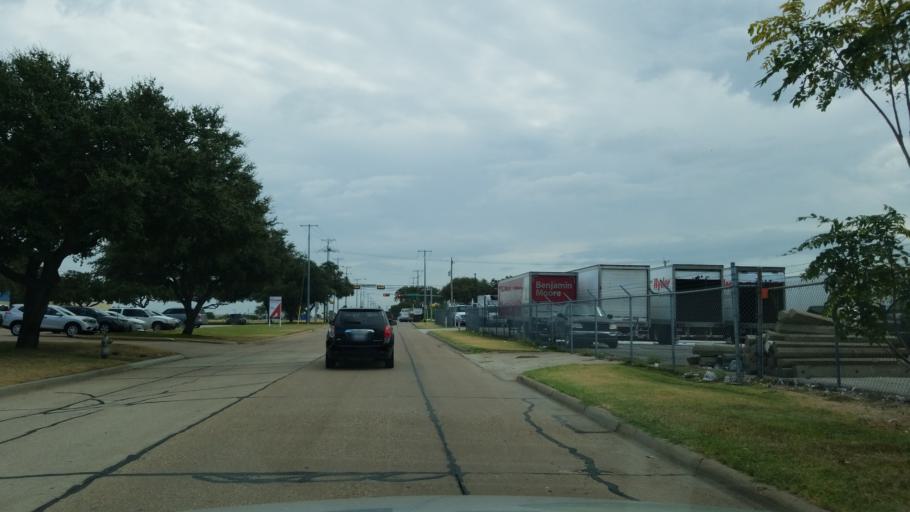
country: US
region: Texas
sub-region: Dallas County
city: Garland
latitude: 32.9017
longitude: -96.6844
